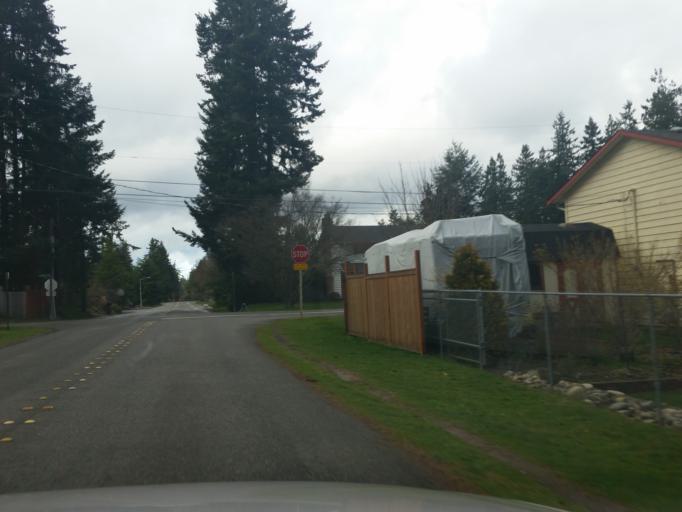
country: US
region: Washington
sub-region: Snohomish County
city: Meadowdale
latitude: 47.8604
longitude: -122.3091
